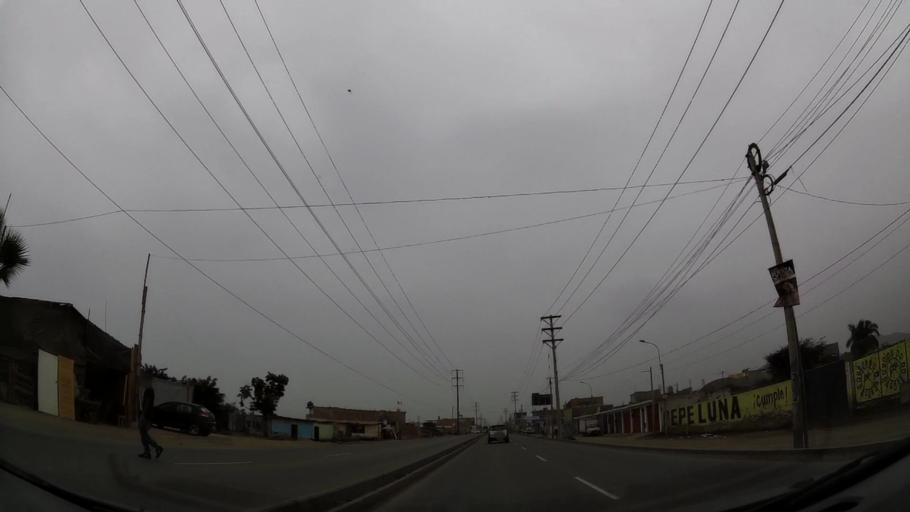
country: PE
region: Lima
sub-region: Lima
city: Punta Hermosa
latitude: -12.2810
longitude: -76.8666
